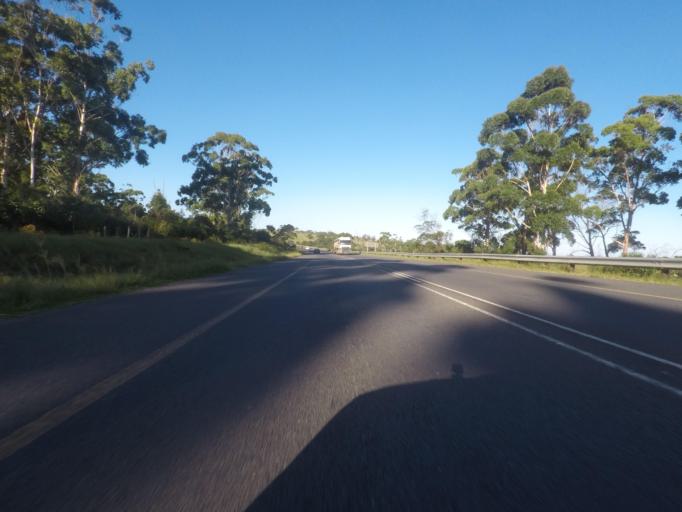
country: ZA
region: Eastern Cape
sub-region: Buffalo City Metropolitan Municipality
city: East London
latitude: -33.0450
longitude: 27.8263
